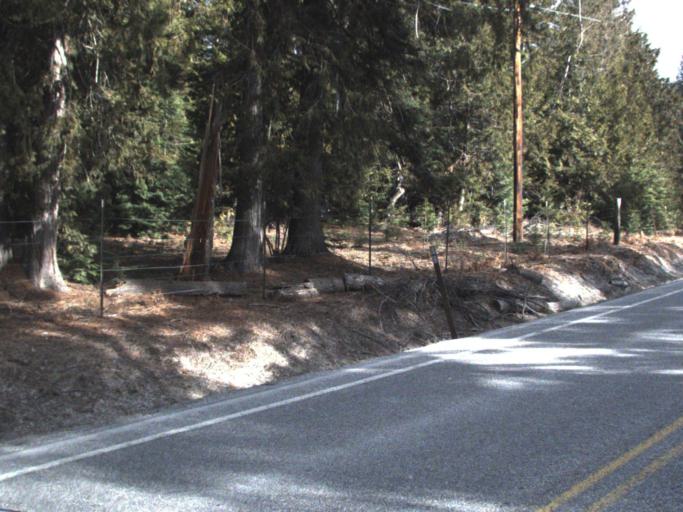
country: US
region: Washington
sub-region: Pend Oreille County
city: Newport
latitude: 48.4422
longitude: -117.3223
